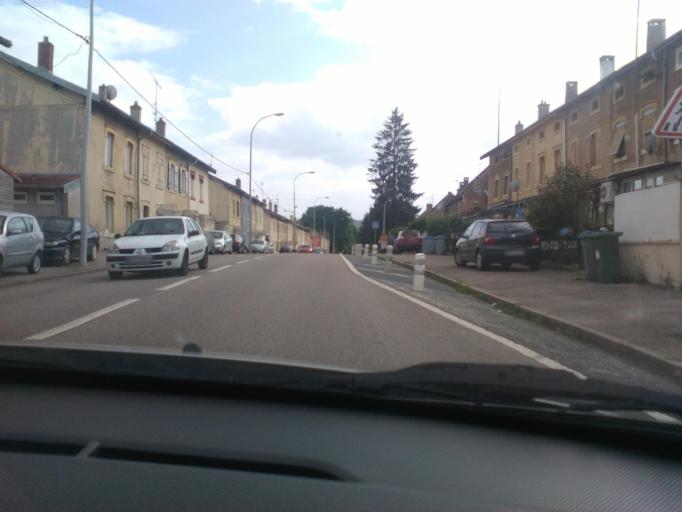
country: FR
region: Lorraine
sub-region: Departement de Meurthe-et-Moselle
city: Pompey
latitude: 48.7755
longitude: 6.1308
